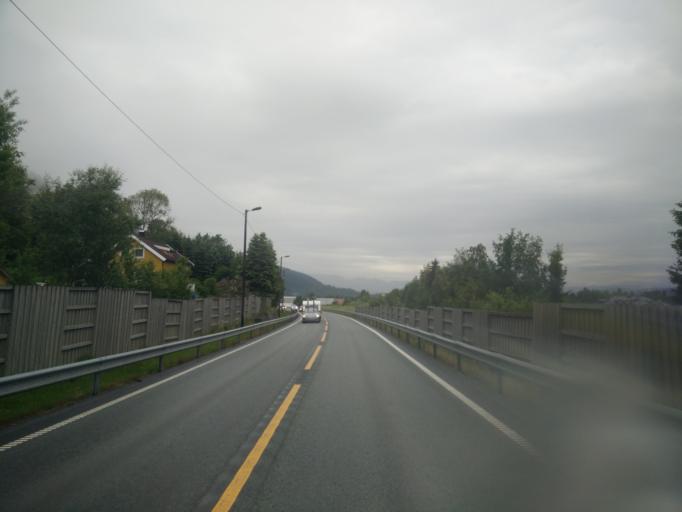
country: NO
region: Sor-Trondelag
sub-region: Orkdal
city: Orkanger
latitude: 63.3043
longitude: 9.8528
